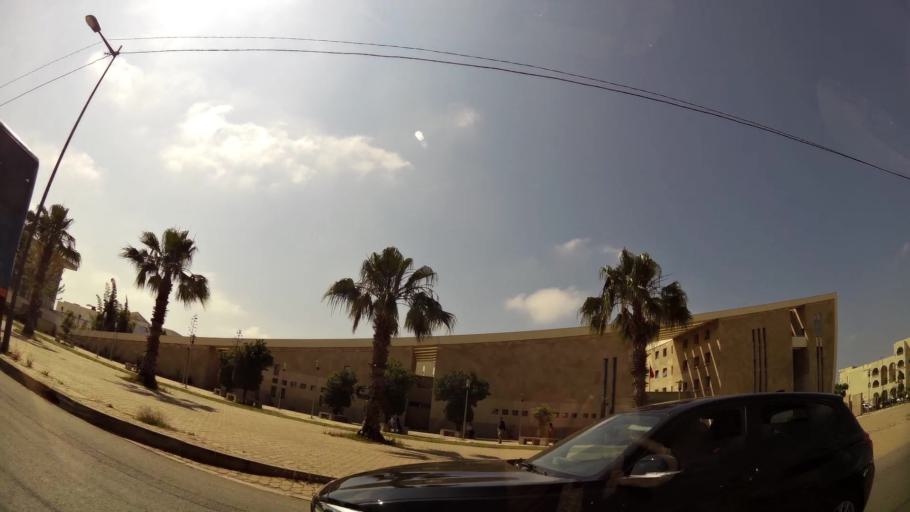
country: MA
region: Rabat-Sale-Zemmour-Zaer
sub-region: Rabat
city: Rabat
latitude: 33.9749
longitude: -6.8705
